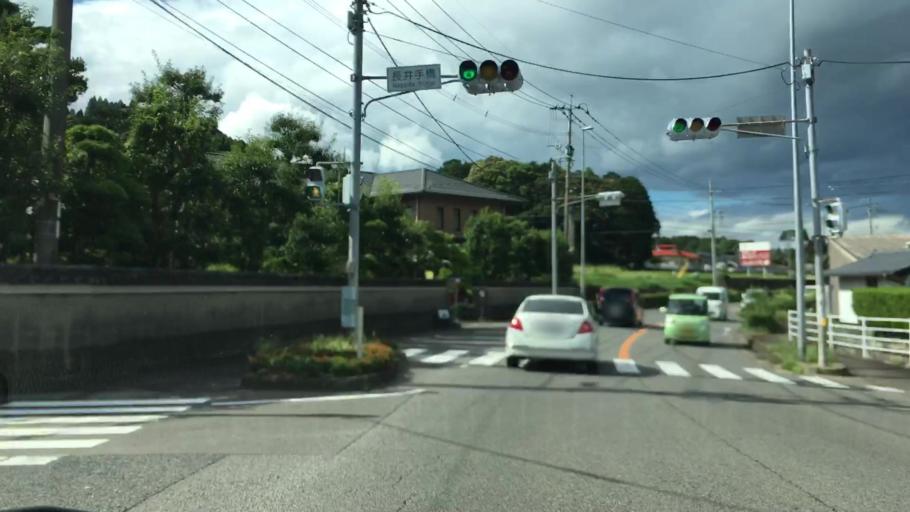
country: JP
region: Saga Prefecture
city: Imaricho-ko
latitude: 33.2418
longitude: 129.8504
